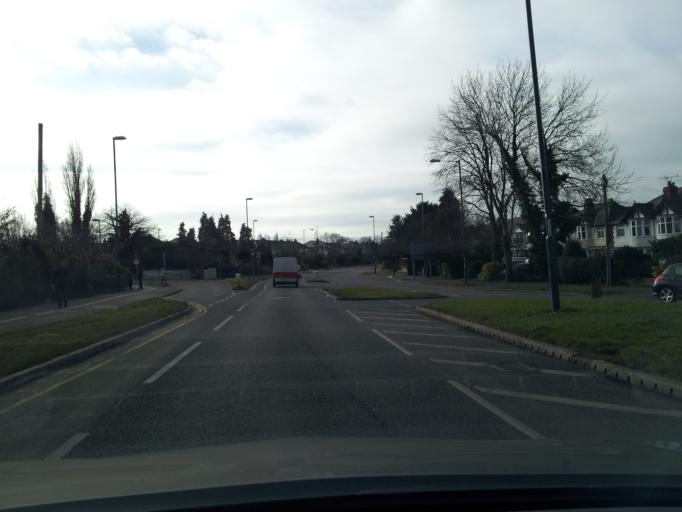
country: GB
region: England
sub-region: Derby
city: Derby
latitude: 52.9114
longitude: -1.5166
